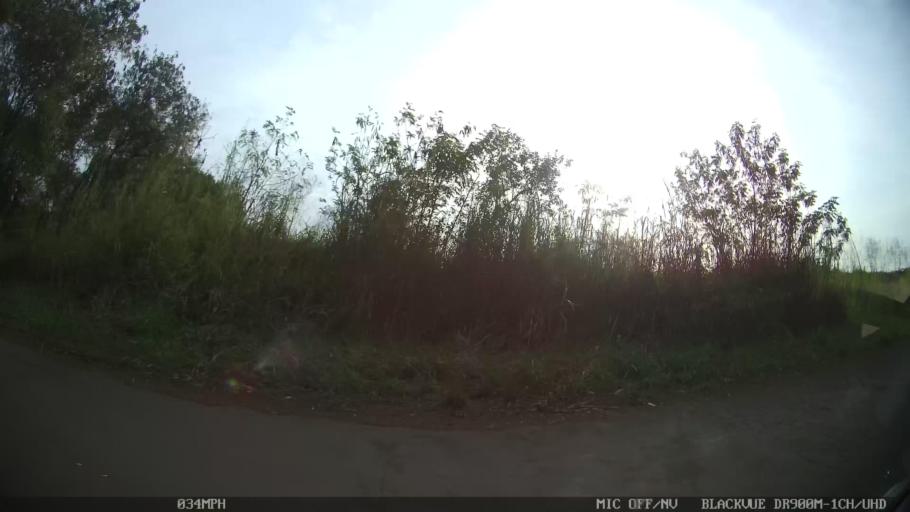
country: BR
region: Sao Paulo
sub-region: Piracicaba
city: Piracicaba
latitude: -22.6989
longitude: -47.5882
